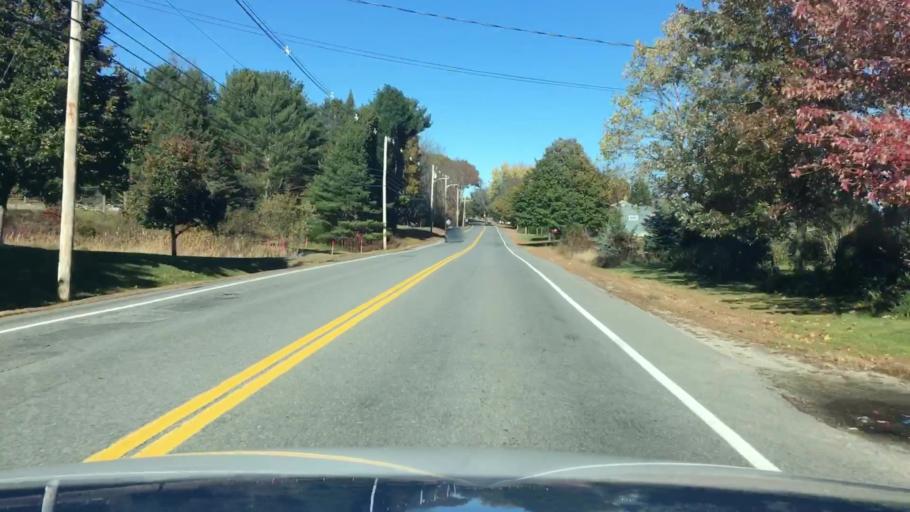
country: US
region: Maine
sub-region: Cumberland County
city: Falmouth
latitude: 43.7204
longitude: -70.2482
